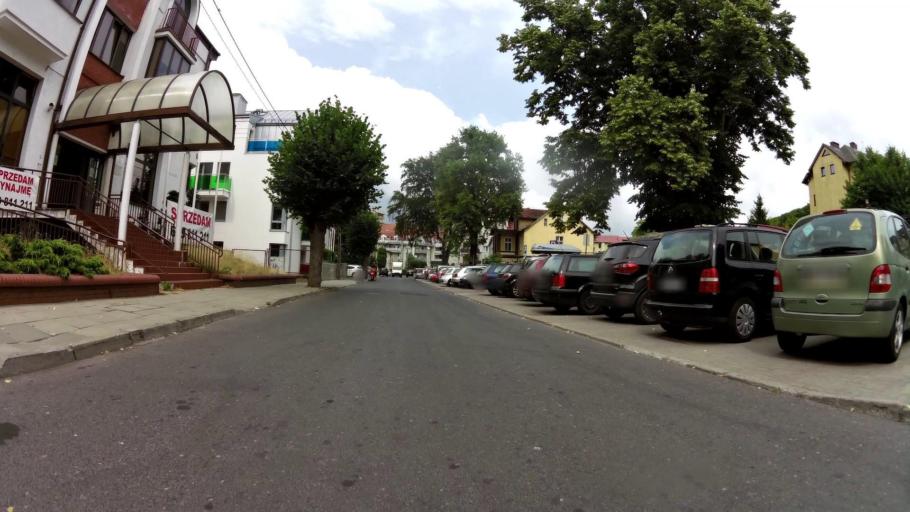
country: PL
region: West Pomeranian Voivodeship
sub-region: Powiat kamienski
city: Miedzyzdroje
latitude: 53.9310
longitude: 14.4517
